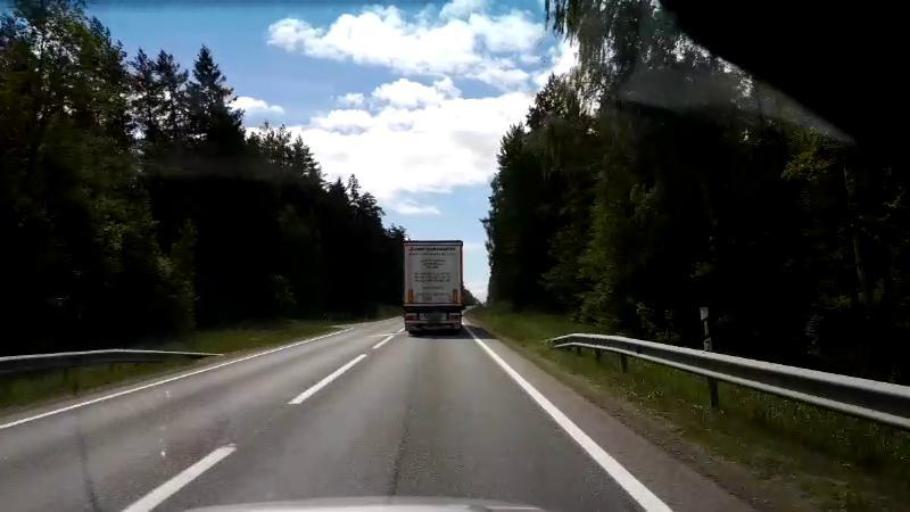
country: LV
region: Salacgrivas
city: Salacgriva
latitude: 57.5640
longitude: 24.4342
